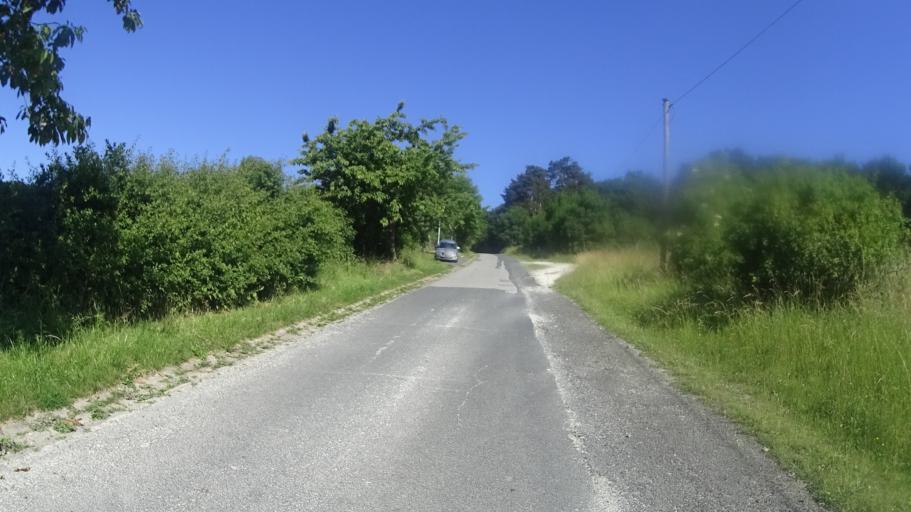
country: DE
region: Lower Saxony
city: Elbe
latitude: 52.0961
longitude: 10.2625
